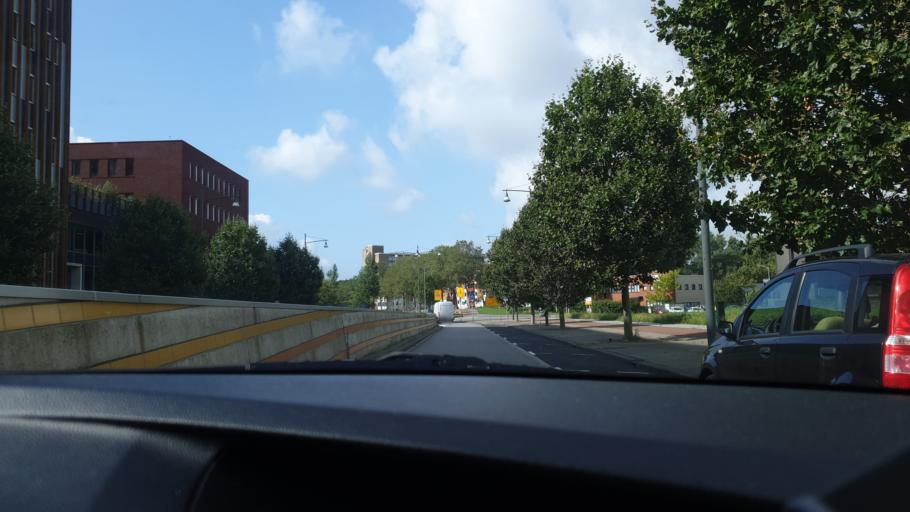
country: NL
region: South Holland
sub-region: Gemeente Dordrecht
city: Dordrecht
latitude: 51.7923
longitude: 4.6807
